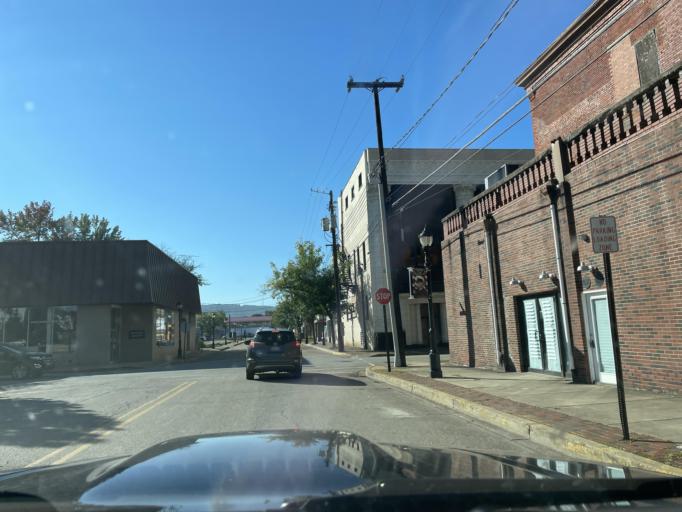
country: US
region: Pennsylvania
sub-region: Westmoreland County
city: New Kensington
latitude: 40.5657
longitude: -79.7647
